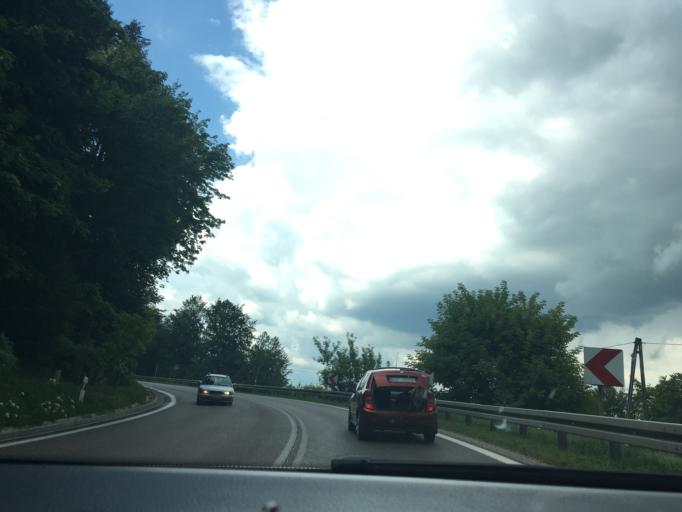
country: PL
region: Subcarpathian Voivodeship
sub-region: Powiat brzozowski
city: Jablonica Polska
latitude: 49.7251
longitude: 21.9095
